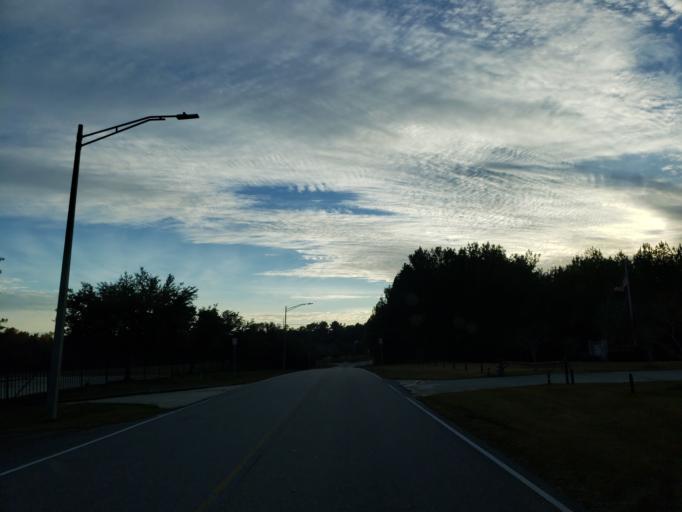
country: US
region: Mississippi
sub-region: Forrest County
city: Hattiesburg
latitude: 31.2577
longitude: -89.2776
